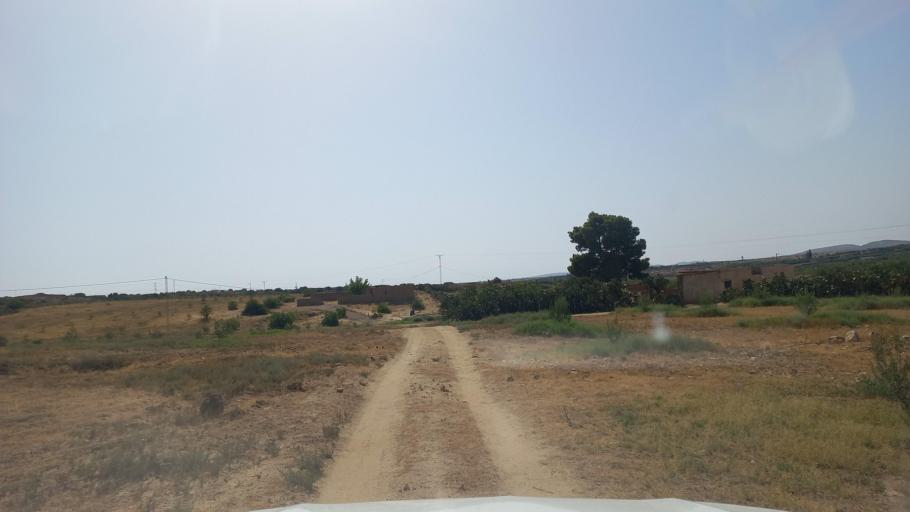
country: TN
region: Al Qasrayn
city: Kasserine
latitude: 35.2268
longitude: 9.0506
